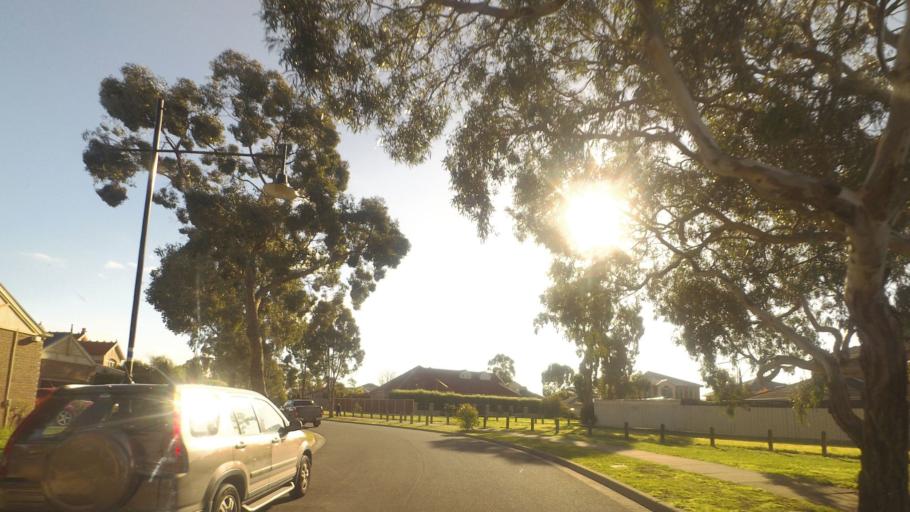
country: AU
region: Victoria
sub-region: Banyule
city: Watsonia North
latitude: -37.6945
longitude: 145.0750
